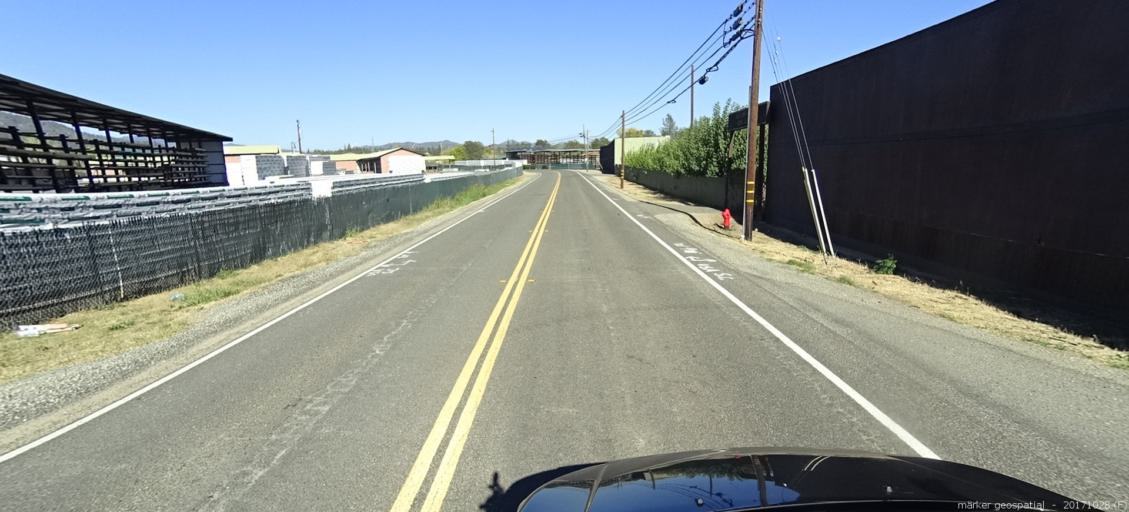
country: US
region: California
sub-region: Shasta County
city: Shasta
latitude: 40.6035
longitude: -122.4636
